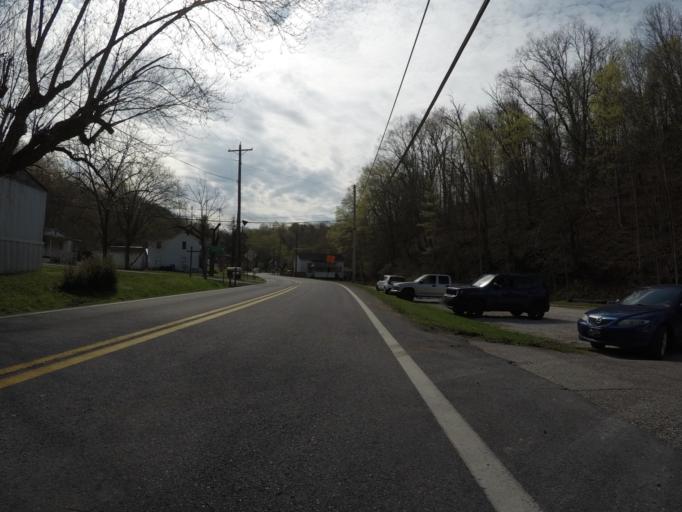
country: US
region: West Virginia
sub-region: Cabell County
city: Pea Ridge
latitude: 38.3767
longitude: -82.3725
